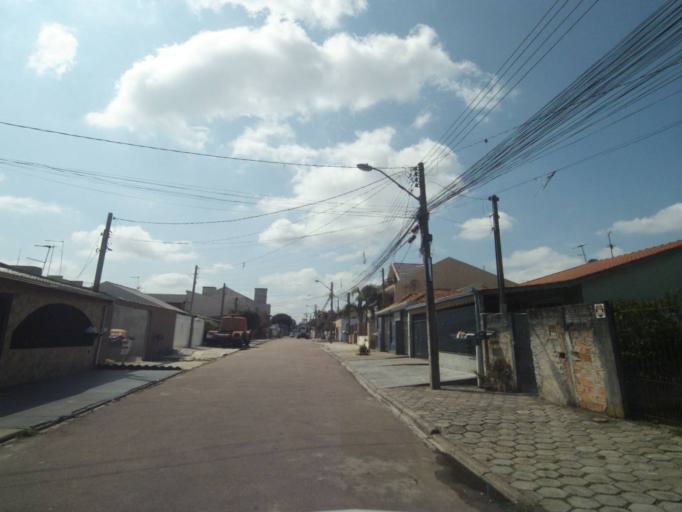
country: BR
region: Parana
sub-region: Sao Jose Dos Pinhais
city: Sao Jose dos Pinhais
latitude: -25.5404
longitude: -49.2686
